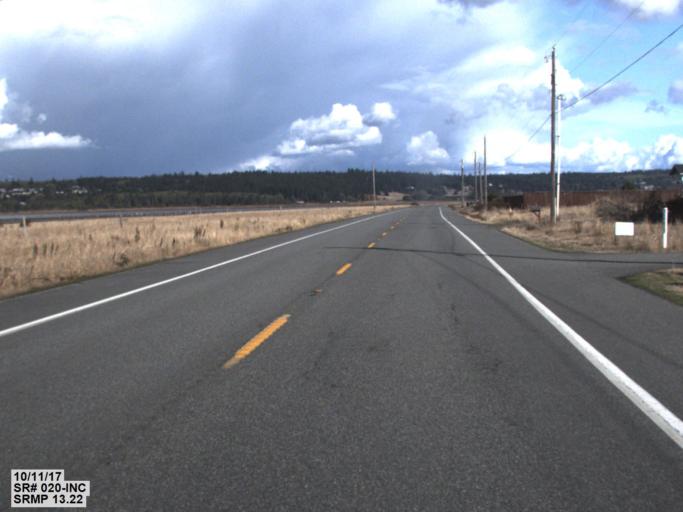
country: US
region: Washington
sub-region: Island County
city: Coupeville
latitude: 48.1609
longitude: -122.6666
